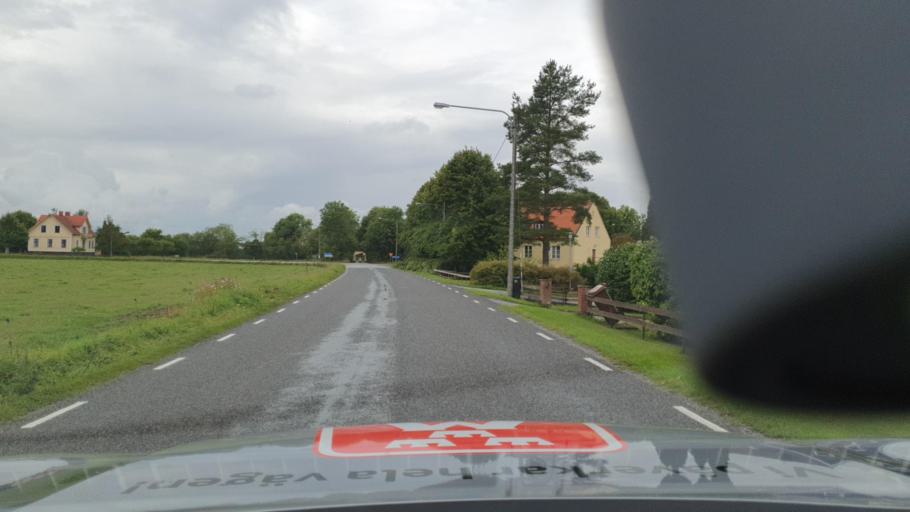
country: SE
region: Gotland
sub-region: Gotland
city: Visby
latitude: 57.5686
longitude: 18.4648
